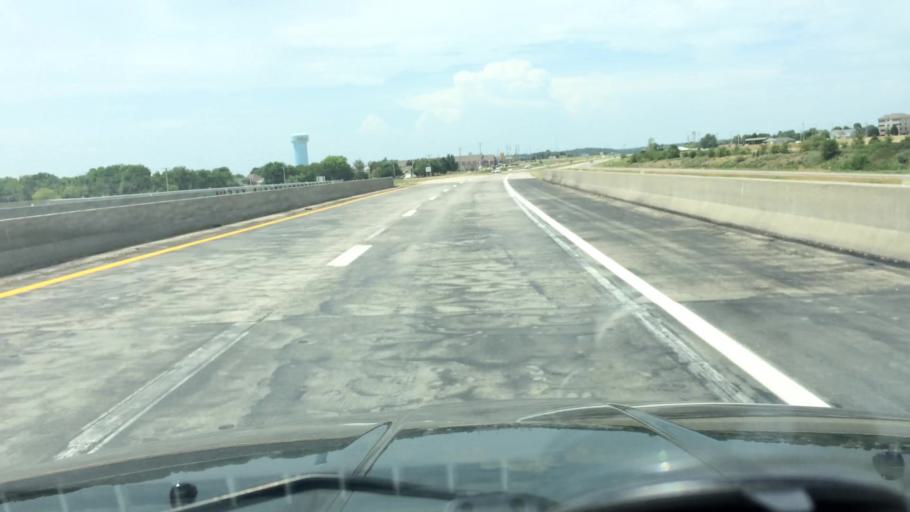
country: US
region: Missouri
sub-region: Polk County
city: Bolivar
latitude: 37.5928
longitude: -93.4319
